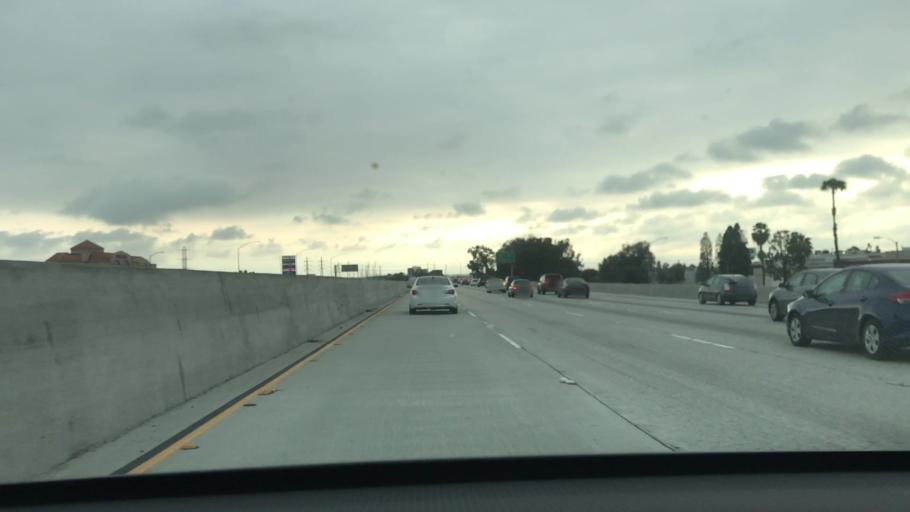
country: US
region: California
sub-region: Los Angeles County
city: West Rancho Dominguez
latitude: 33.8736
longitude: -118.2605
